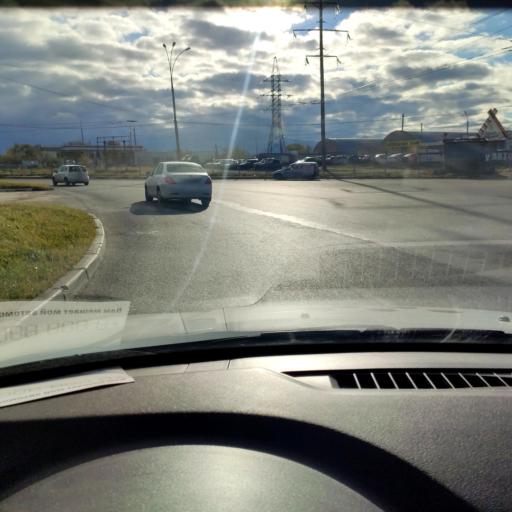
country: RU
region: Samara
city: Tol'yatti
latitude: 53.5308
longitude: 49.2609
